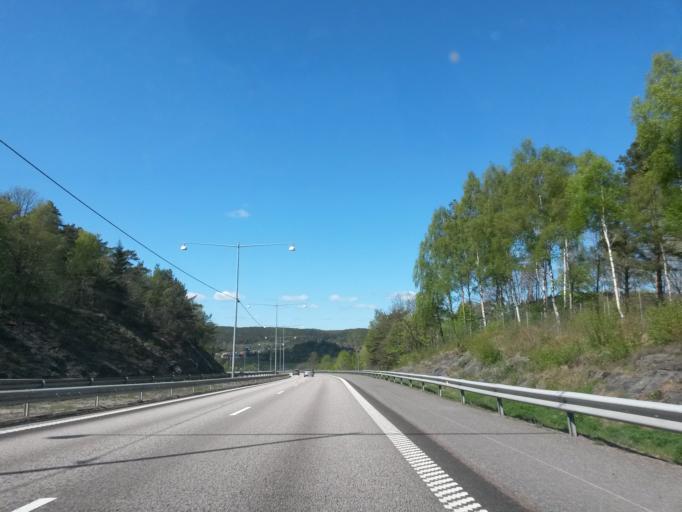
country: SE
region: Vaestra Goetaland
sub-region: Partille Kommun
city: Furulund
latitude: 57.7423
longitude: 12.1669
